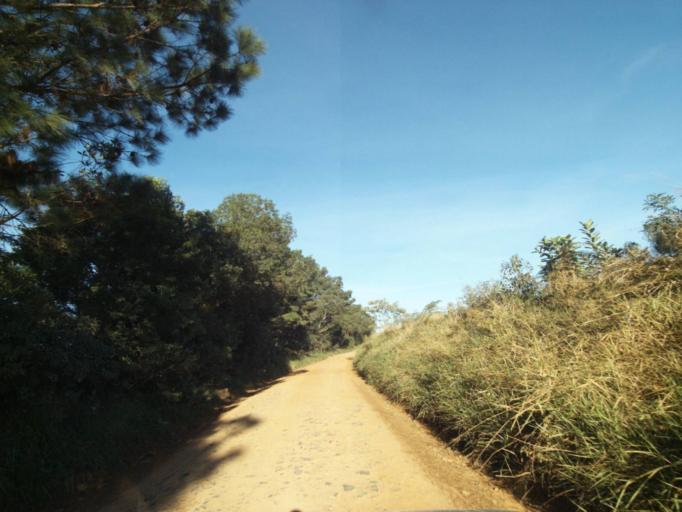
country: BR
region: Parana
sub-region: Telemaco Borba
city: Telemaco Borba
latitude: -24.5291
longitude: -50.6330
